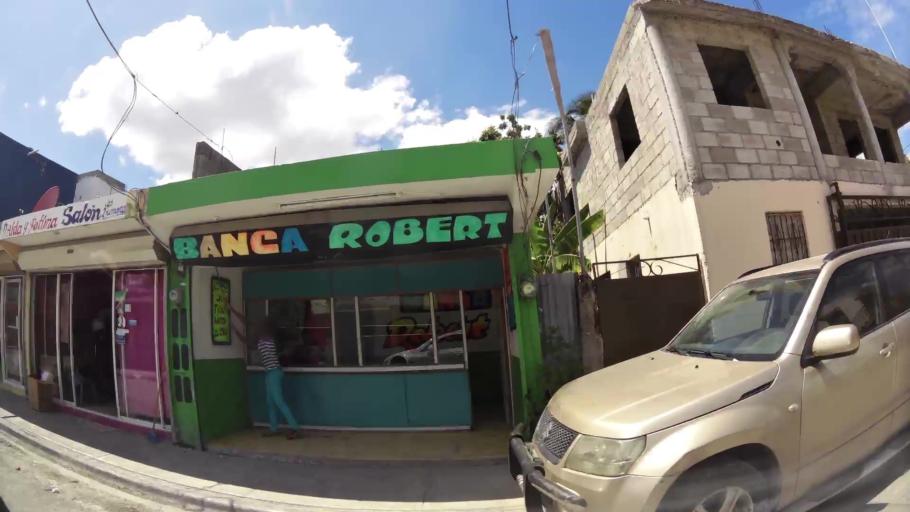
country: DO
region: San Cristobal
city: San Cristobal
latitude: 18.4097
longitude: -70.1027
